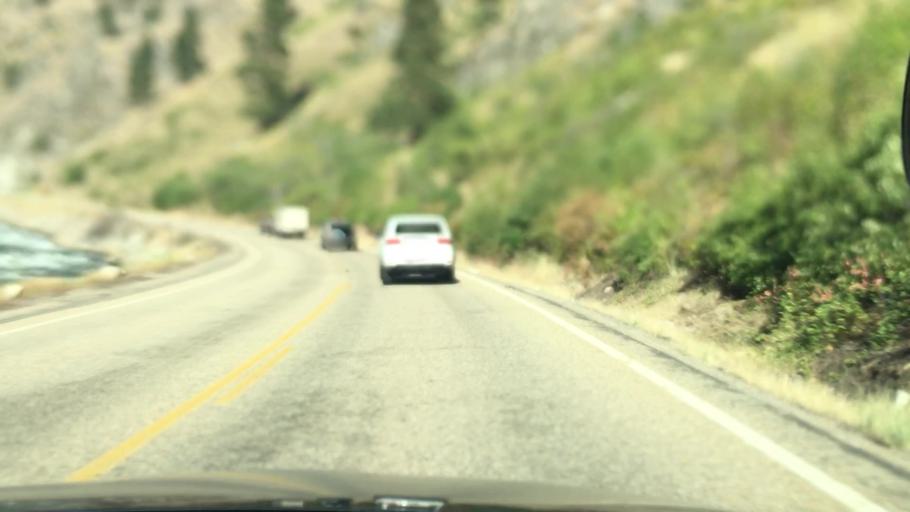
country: US
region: Idaho
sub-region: Boise County
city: Idaho City
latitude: 44.0891
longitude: -116.1072
